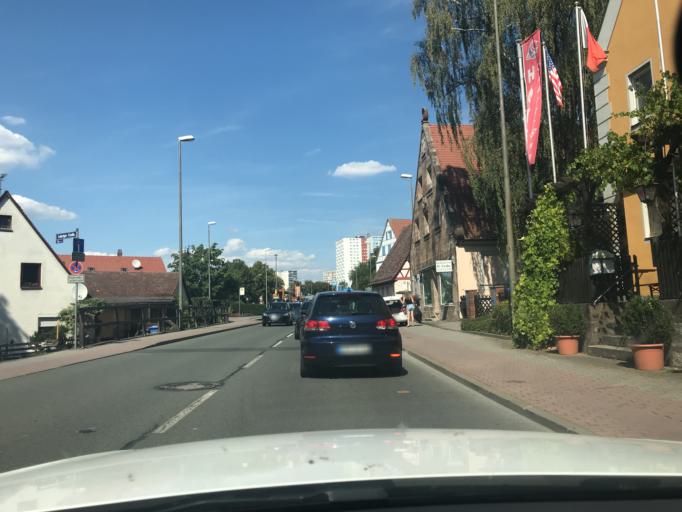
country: DE
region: Bavaria
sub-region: Regierungsbezirk Mittelfranken
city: Erlangen
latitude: 49.5756
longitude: 10.9857
